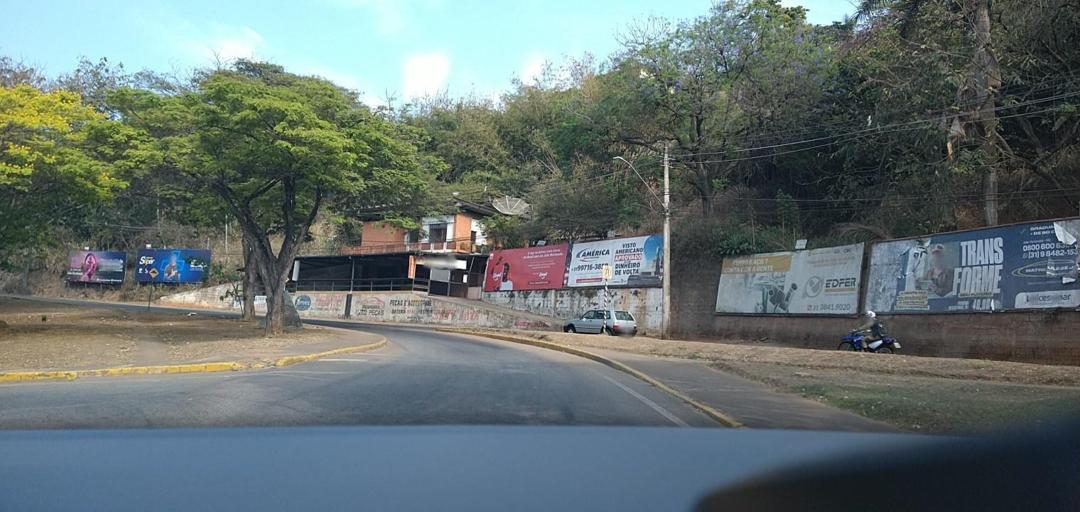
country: BR
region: Minas Gerais
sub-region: Joao Monlevade
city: Joao Monlevade
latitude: -19.8117
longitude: -43.1647
